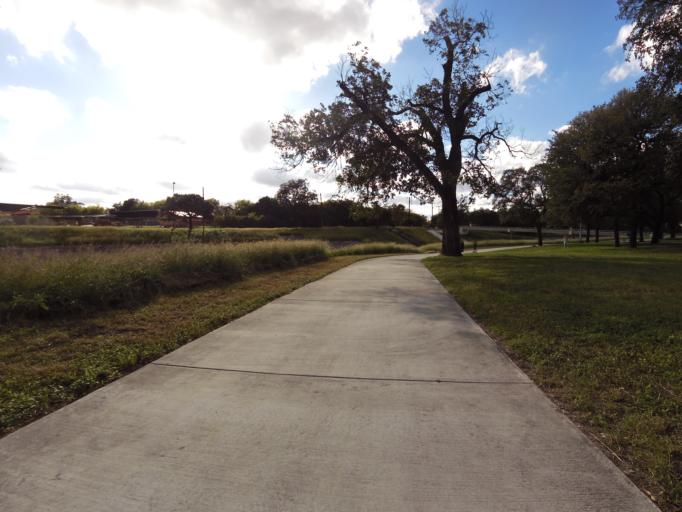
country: US
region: Texas
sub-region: Bexar County
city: San Antonio
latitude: 29.4136
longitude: -98.5296
